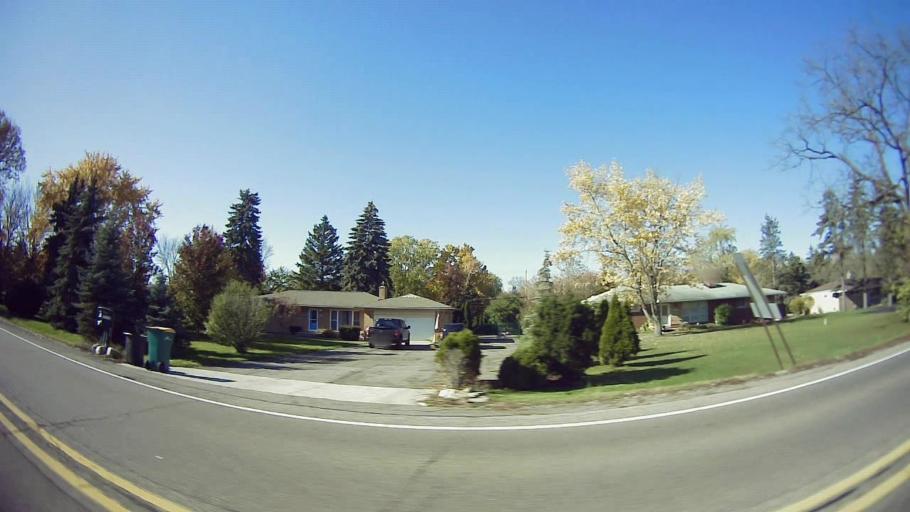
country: US
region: Michigan
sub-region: Oakland County
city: Farmington Hills
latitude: 42.5016
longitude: -83.3783
